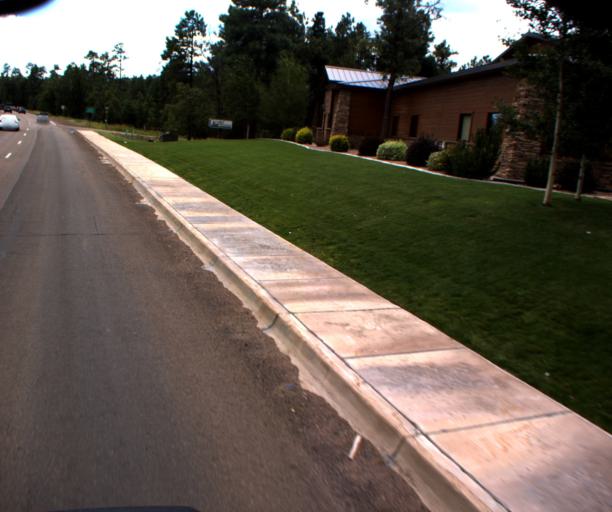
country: US
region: Arizona
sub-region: Navajo County
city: Lake of the Woods
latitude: 34.1843
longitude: -110.0152
